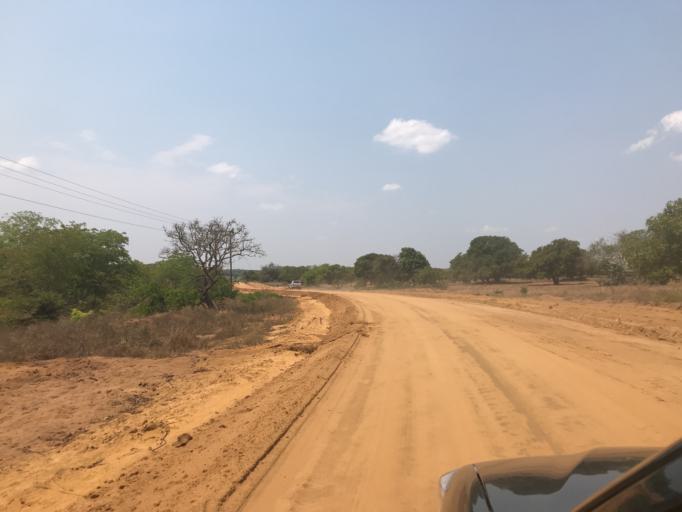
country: MZ
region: Gaza
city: Manjacaze
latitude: -24.5684
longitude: 33.9247
